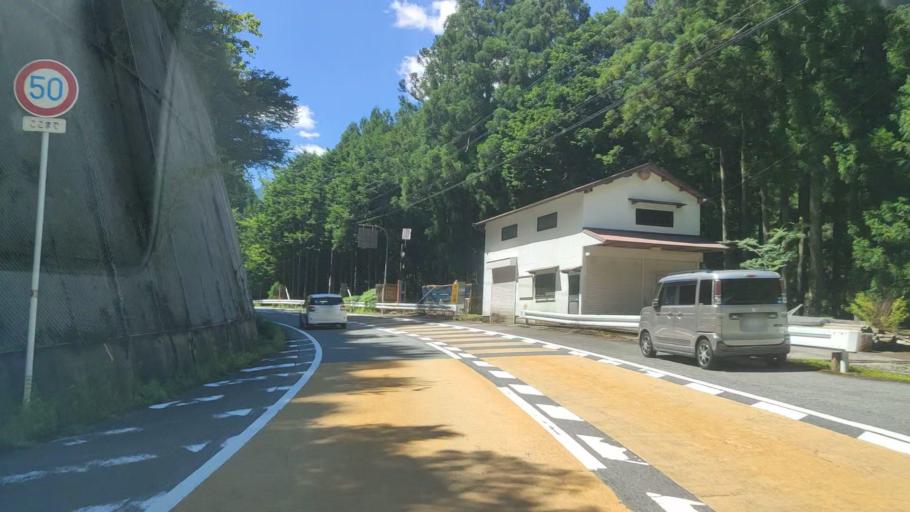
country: JP
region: Mie
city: Owase
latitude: 34.1827
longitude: 136.0055
